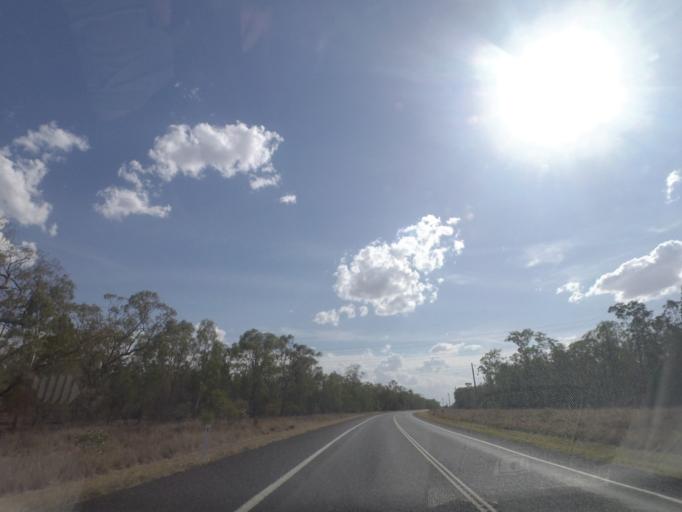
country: AU
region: New South Wales
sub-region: Moree Plains
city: Boggabilla
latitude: -28.5435
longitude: 150.8833
